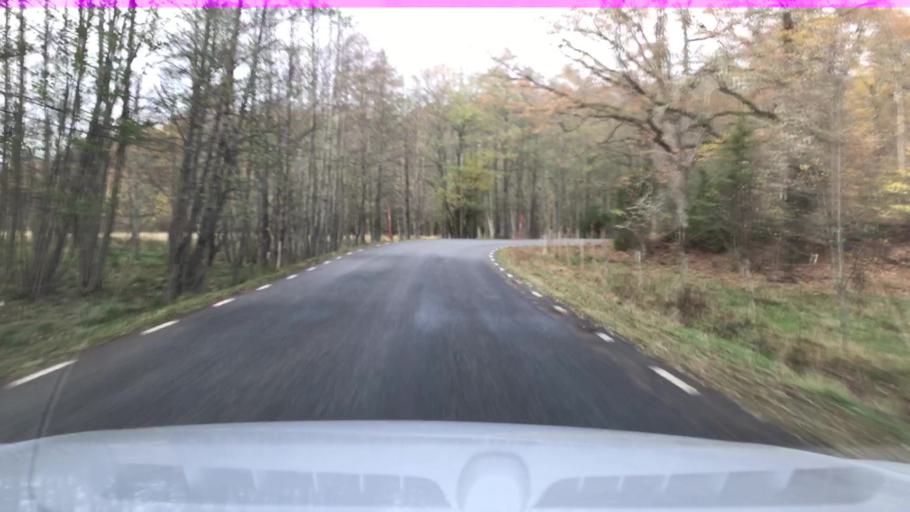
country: SE
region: OEstergoetland
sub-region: Valdemarsviks Kommun
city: Valdemarsvik
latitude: 58.2887
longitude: 16.7635
